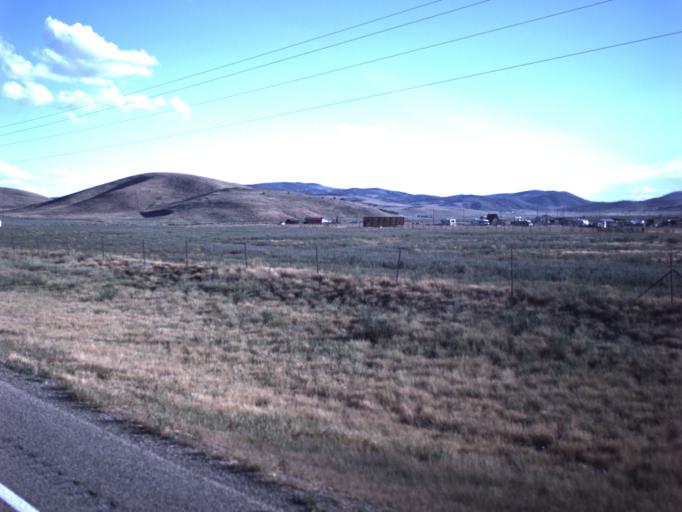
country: US
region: Utah
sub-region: Sanpete County
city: Fairview
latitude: 39.7711
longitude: -111.4876
